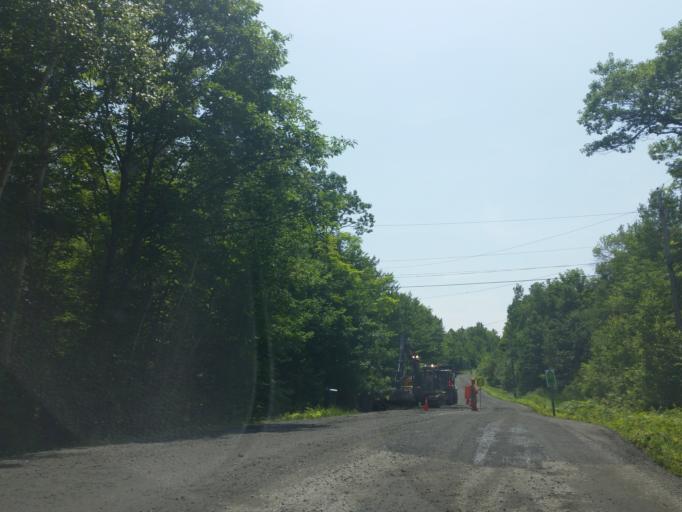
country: CA
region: Ontario
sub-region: Parry Sound District
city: Parry Sound
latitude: 45.4404
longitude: -80.0078
